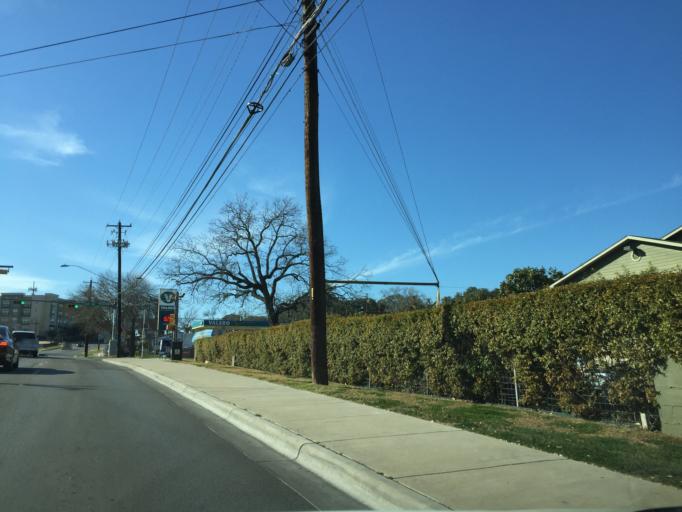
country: US
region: Texas
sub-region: Travis County
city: Austin
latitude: 30.2367
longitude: -97.7481
